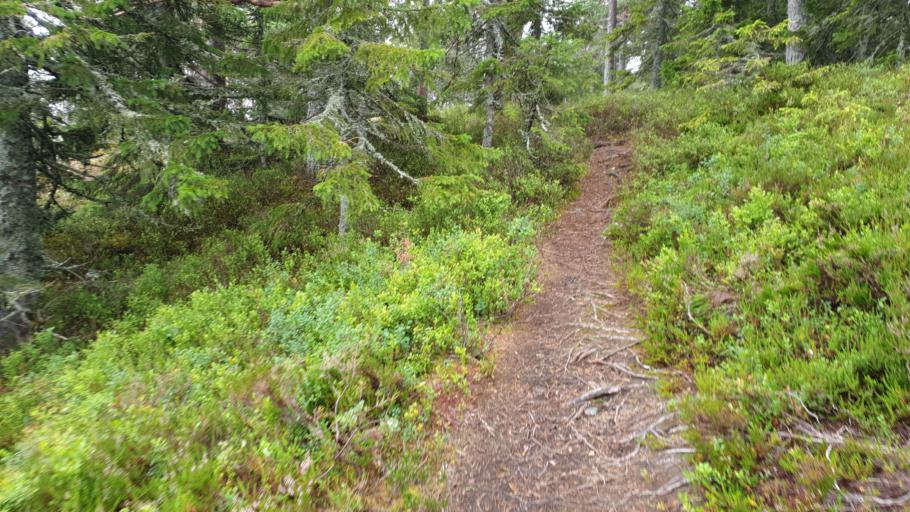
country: SE
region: Gaevleborg
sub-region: Hudiksvalls Kommun
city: Sorforsa
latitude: 61.6471
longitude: 16.7640
